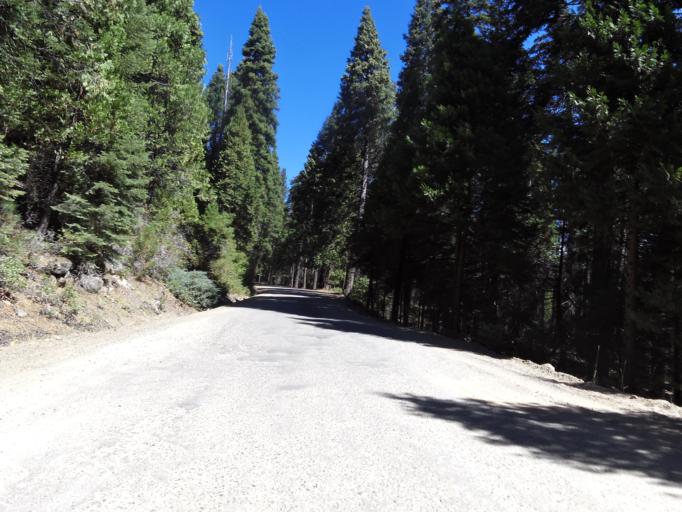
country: US
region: California
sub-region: Madera County
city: Oakhurst
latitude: 37.4294
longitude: -119.5462
